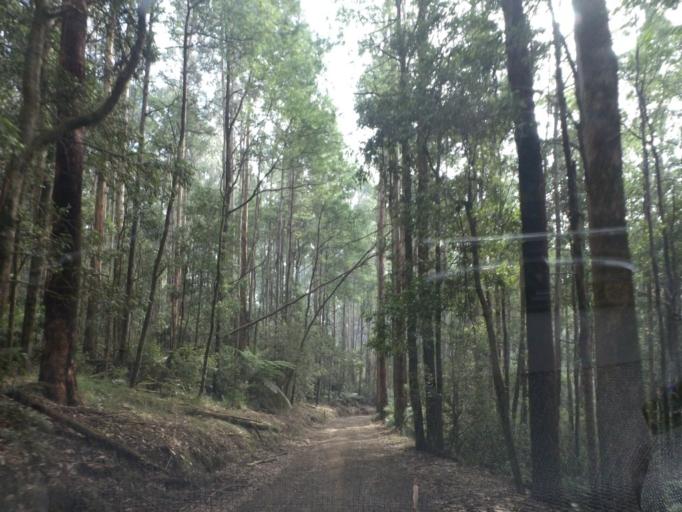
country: AU
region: Victoria
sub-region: Yarra Ranges
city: Healesville
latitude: -37.5727
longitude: 145.5790
